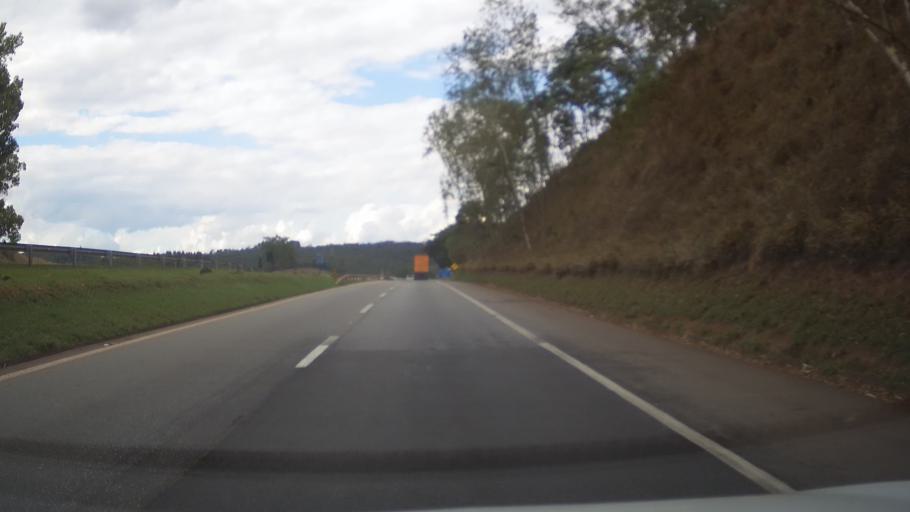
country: BR
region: Minas Gerais
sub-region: Itauna
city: Itauna
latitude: -20.2921
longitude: -44.4365
